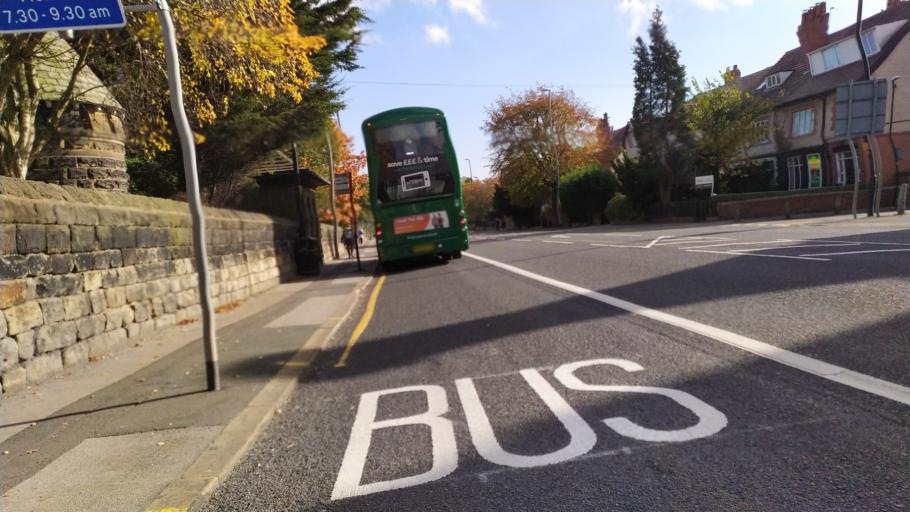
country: GB
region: England
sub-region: City and Borough of Leeds
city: Horsforth
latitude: 53.8331
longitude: -1.5925
